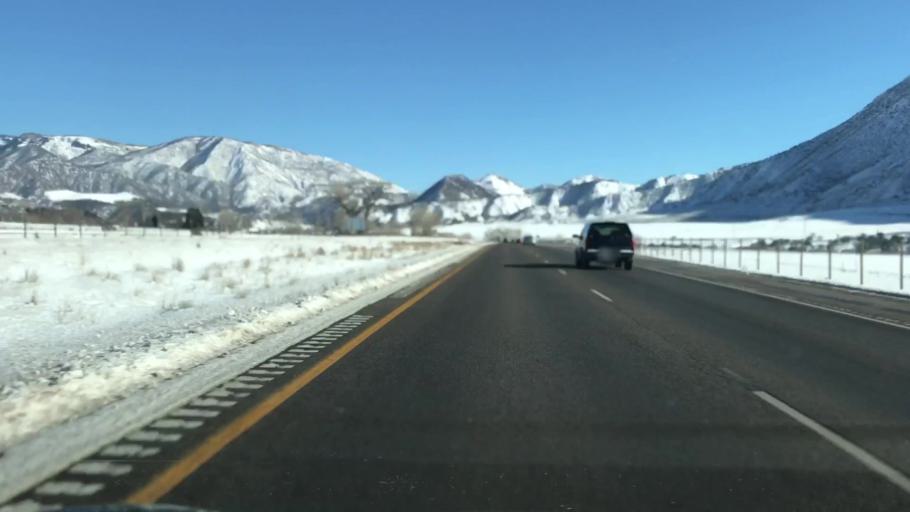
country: US
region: Colorado
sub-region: Garfield County
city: New Castle
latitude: 39.5658
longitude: -107.4997
